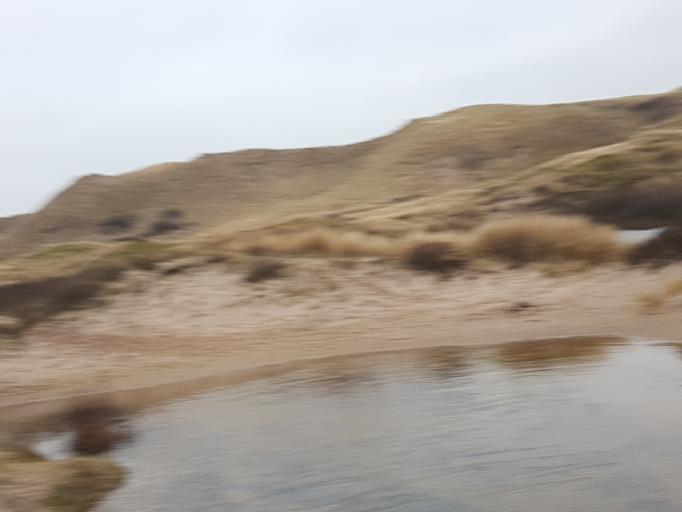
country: NL
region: North Holland
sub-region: Gemeente Bergen
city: Egmond aan Zee
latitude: 52.6369
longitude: 4.6278
